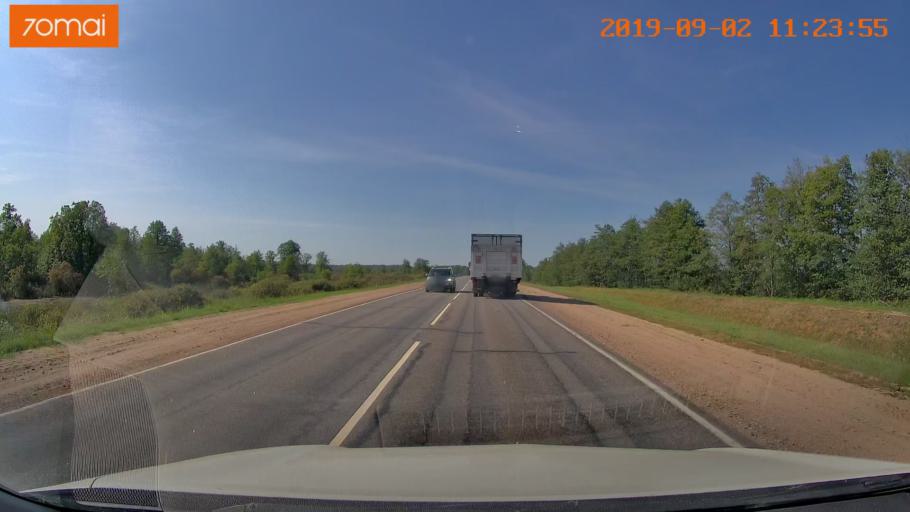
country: RU
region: Smolensk
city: Roslavl'
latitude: 54.0138
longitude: 32.9838
